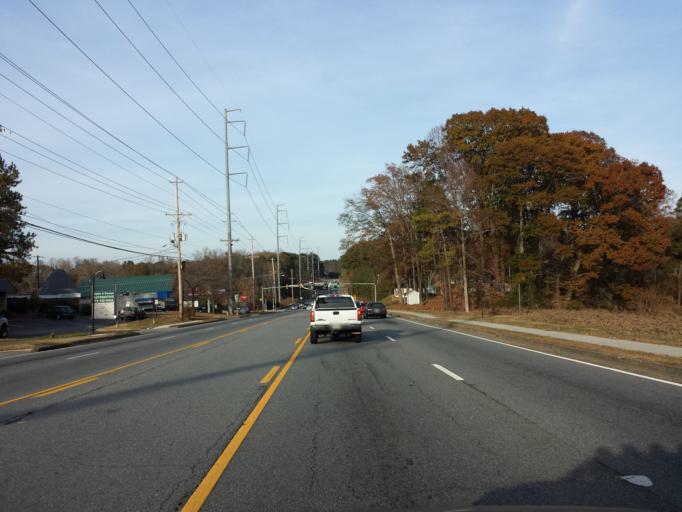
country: US
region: Georgia
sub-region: Cherokee County
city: Woodstock
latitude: 34.0479
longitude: -84.5281
